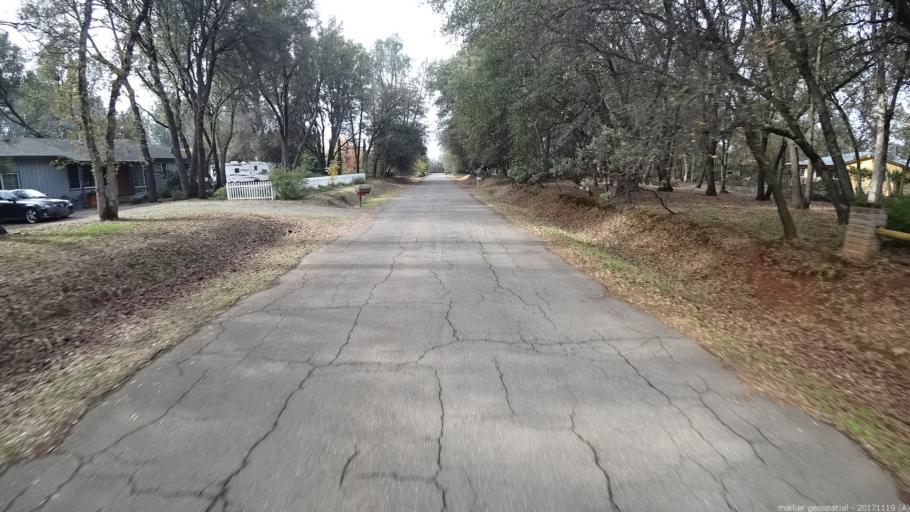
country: US
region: California
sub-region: Shasta County
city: Anderson
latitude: 40.4894
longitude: -122.2718
